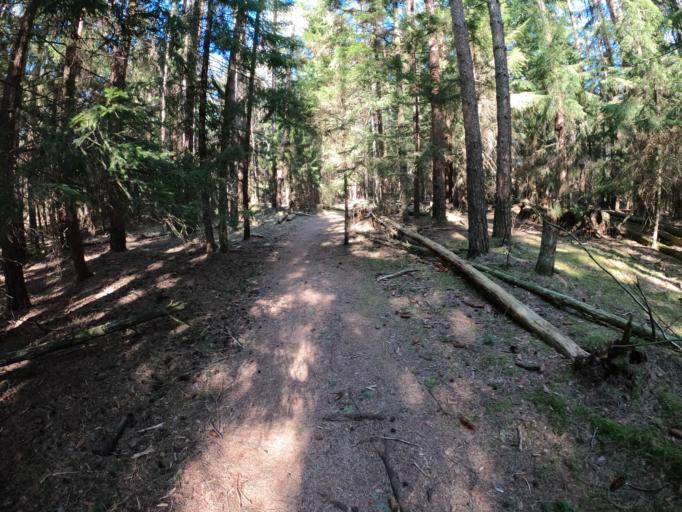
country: SE
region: Vaestra Goetaland
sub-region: Harryda Kommun
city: Molnlycke
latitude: 57.6417
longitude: 12.1174
